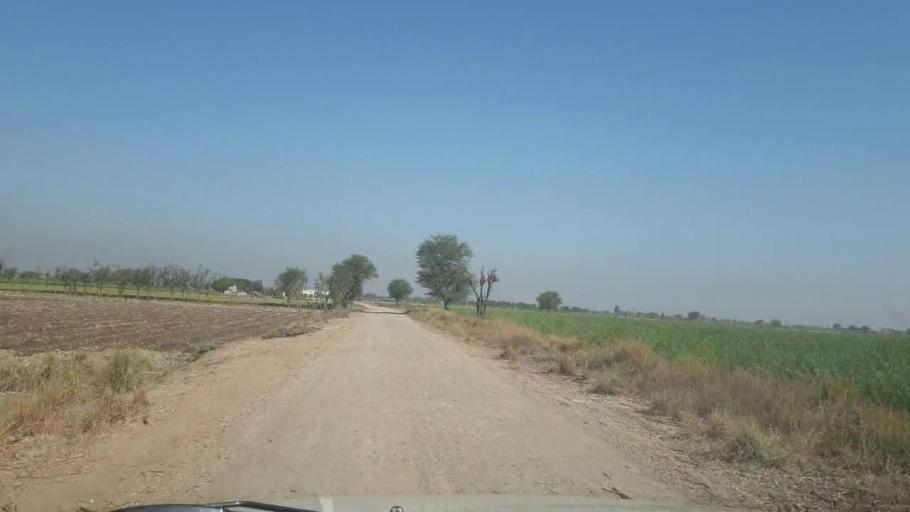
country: PK
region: Sindh
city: Mirpur Khas
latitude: 25.5068
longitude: 69.1476
